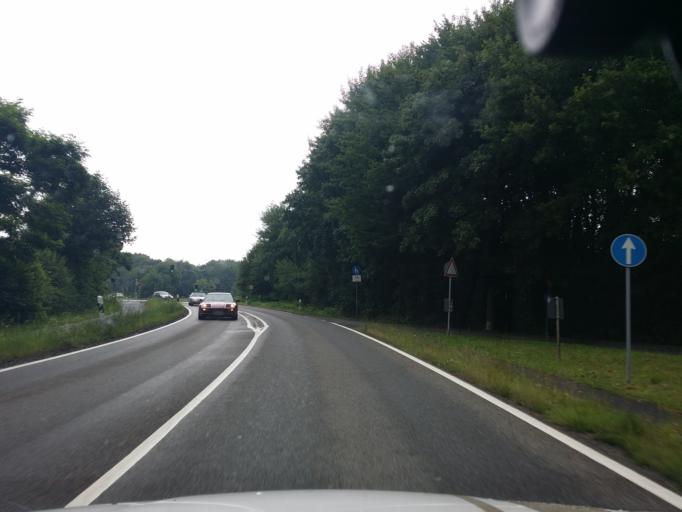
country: DE
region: Hesse
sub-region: Regierungsbezirk Darmstadt
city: Konigstein im Taunus
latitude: 50.1852
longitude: 8.4853
